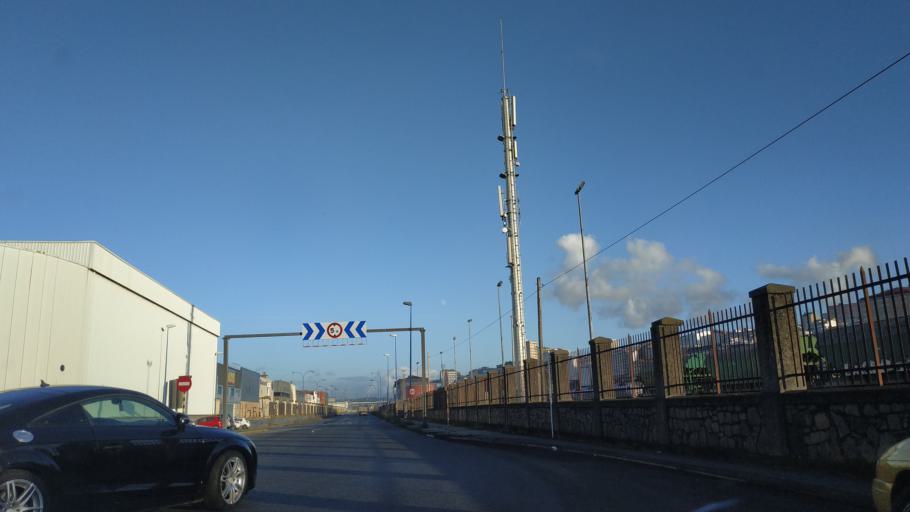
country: ES
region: Galicia
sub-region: Provincia da Coruna
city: A Coruna
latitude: 43.3582
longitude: -8.3973
